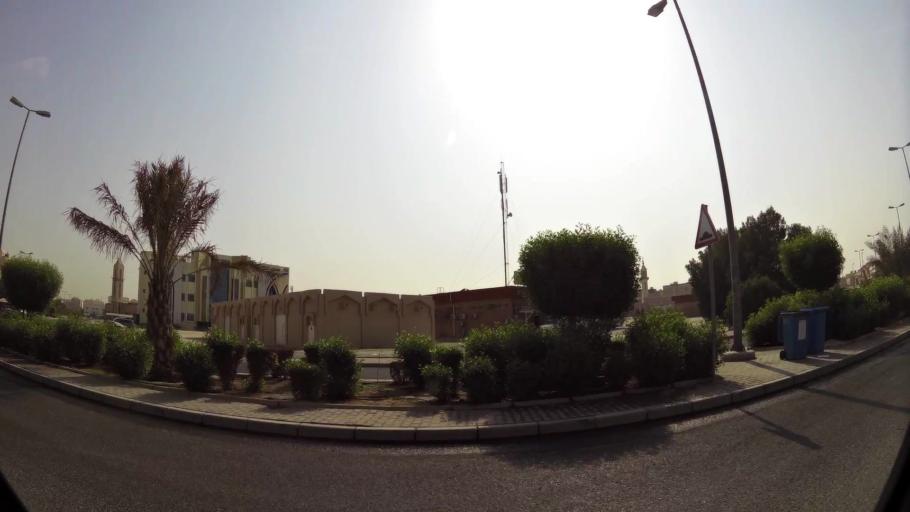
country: KW
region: Al Asimah
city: Ar Rabiyah
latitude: 29.2725
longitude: 47.8909
